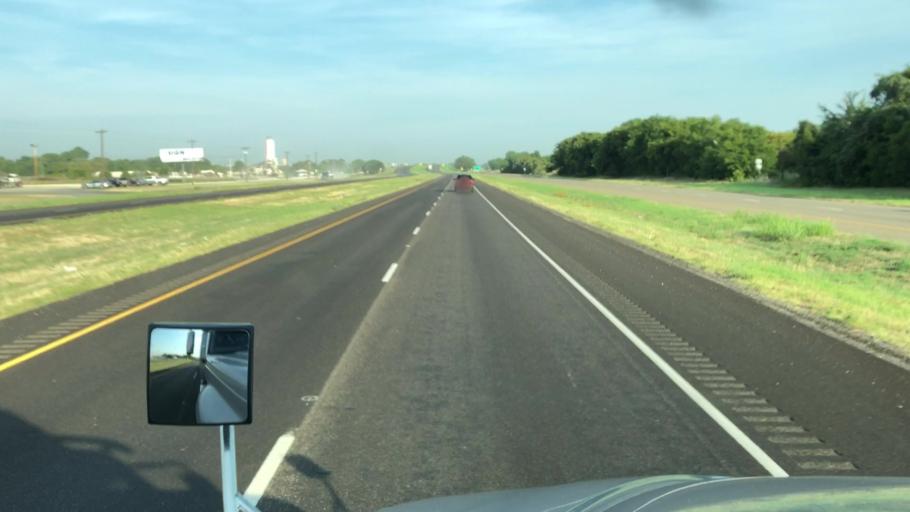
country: US
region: Texas
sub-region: McLennan County
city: Bellmead
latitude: 31.5510
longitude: -97.0815
